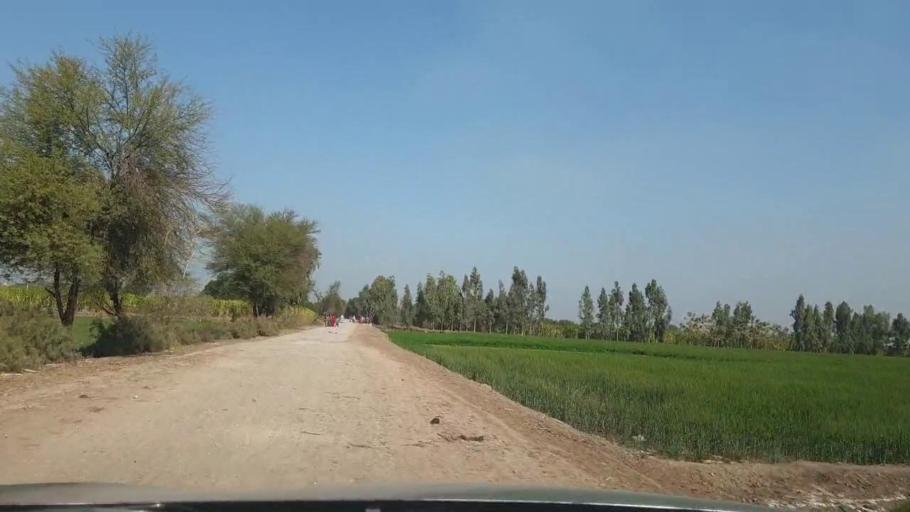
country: PK
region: Sindh
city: Tando Adam
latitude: 25.6086
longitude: 68.6432
